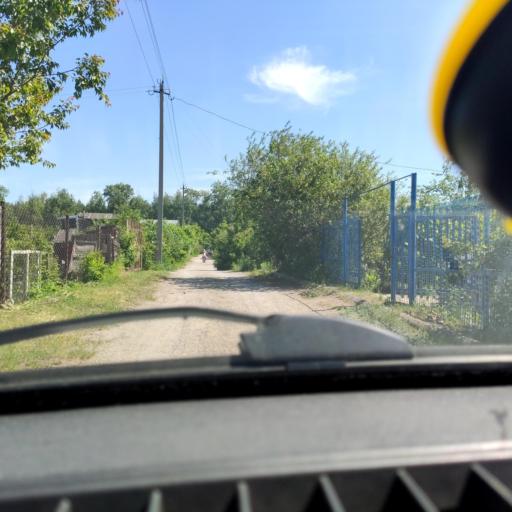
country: RU
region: Samara
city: Povolzhskiy
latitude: 53.6145
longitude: 49.6213
